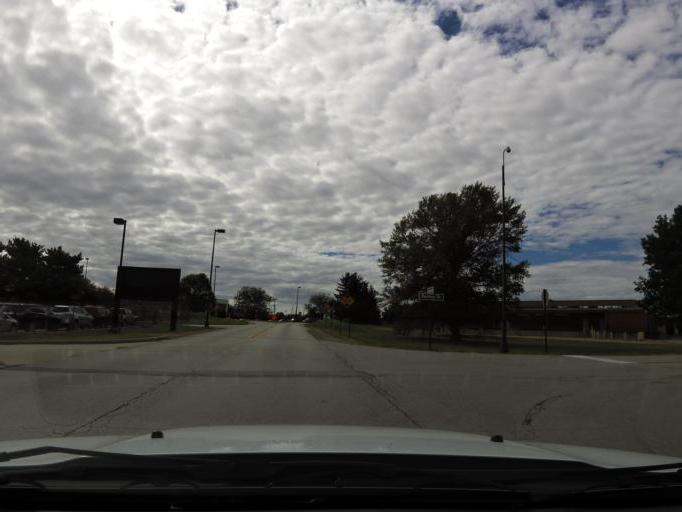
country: US
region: Kentucky
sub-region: Boone County
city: Hebron
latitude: 39.0590
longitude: -84.6617
